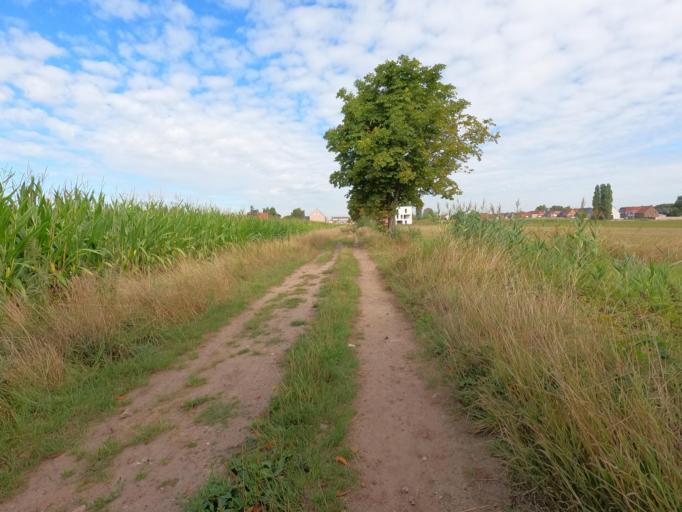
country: BE
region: Flanders
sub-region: Provincie Antwerpen
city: Kapellen
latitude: 51.3012
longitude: 4.4059
